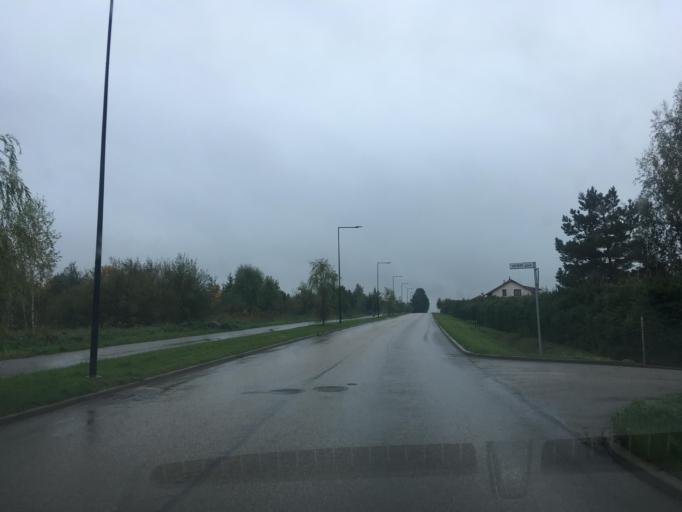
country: EE
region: Tartu
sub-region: UElenurme vald
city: Ulenurme
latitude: 58.3421
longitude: 26.7873
